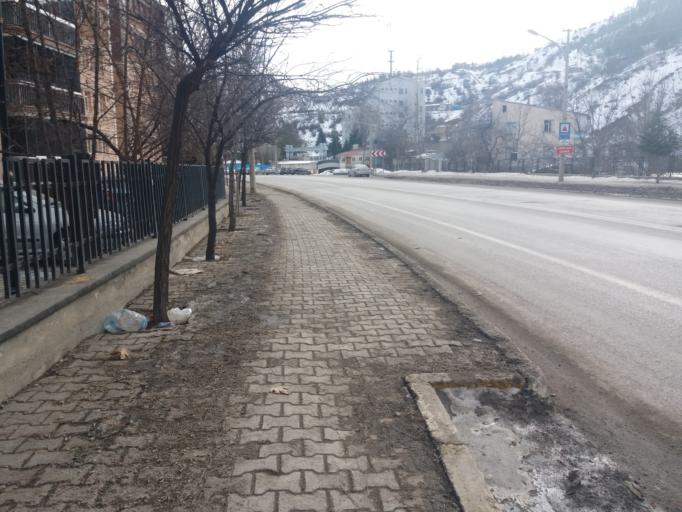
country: TR
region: Gumushane
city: Gumushkhane
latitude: 40.4479
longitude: 39.4975
